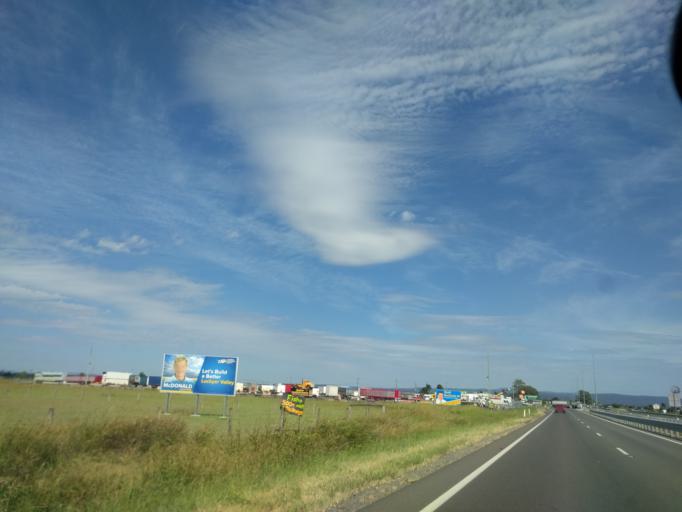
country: AU
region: Queensland
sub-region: Lockyer Valley
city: Gatton
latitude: -27.5456
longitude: 152.3799
